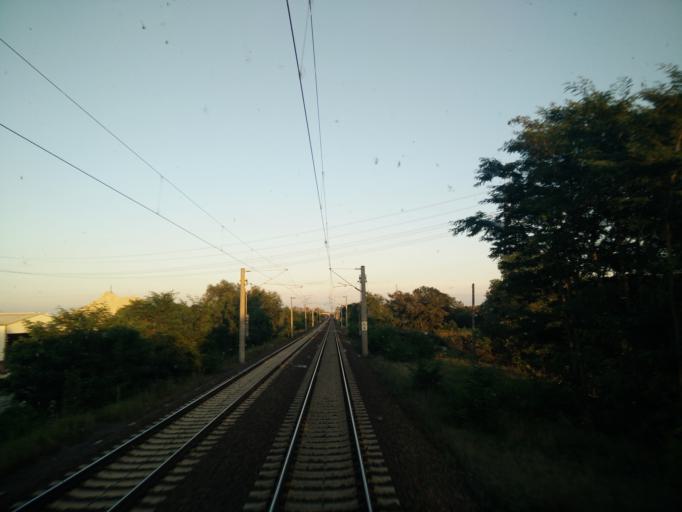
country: DE
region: Brandenburg
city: Wustermark
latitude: 52.5960
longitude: 12.9497
